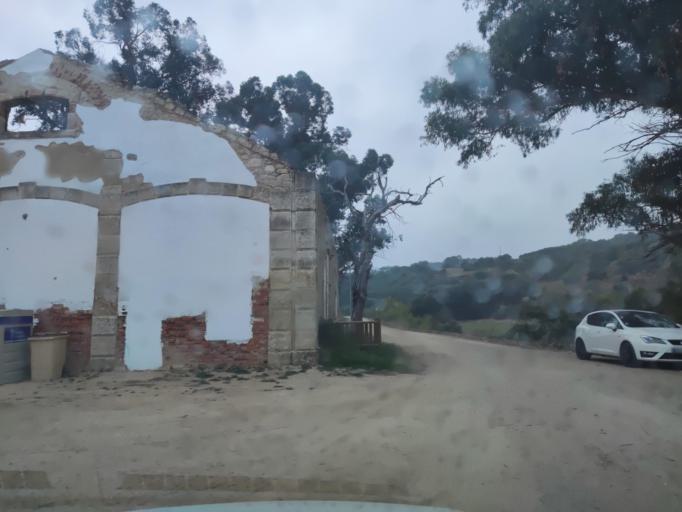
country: ES
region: Castille and Leon
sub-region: Provincia de Salamanca
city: Hinojosa de Duero
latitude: 40.9885
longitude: -6.8379
